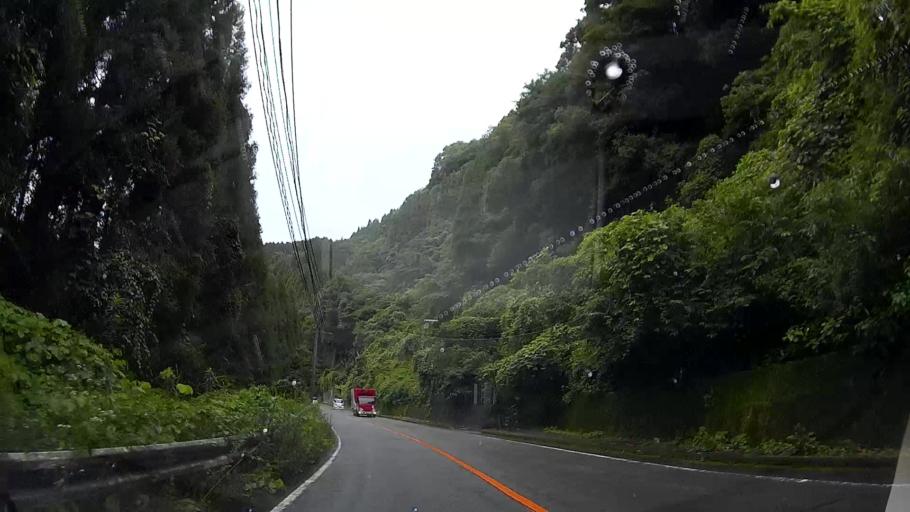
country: JP
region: Oita
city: Tsukawaki
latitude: 33.1670
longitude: 131.0428
